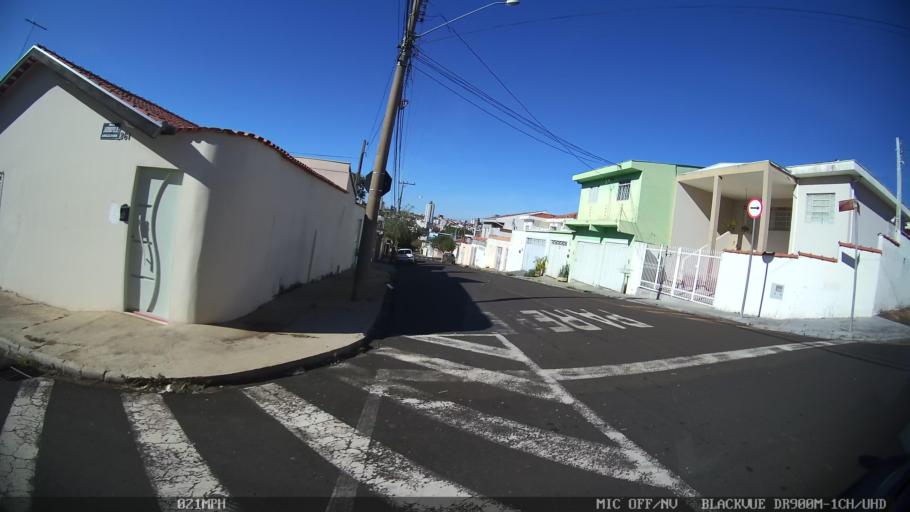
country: BR
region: Sao Paulo
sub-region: Franca
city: Franca
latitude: -20.5419
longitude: -47.4099
